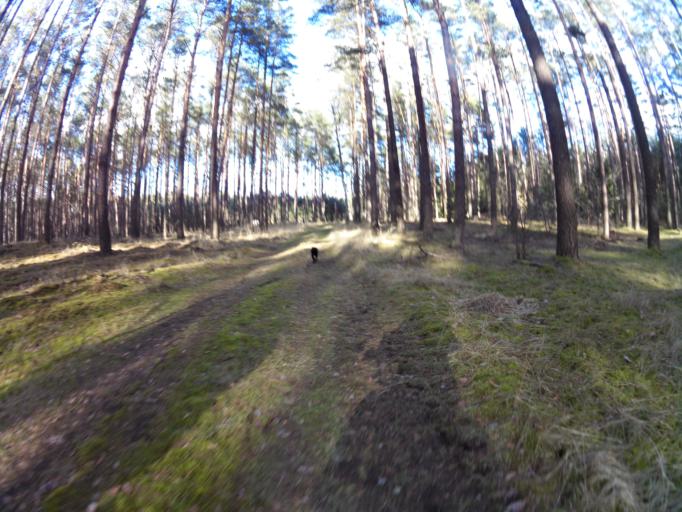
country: PL
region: West Pomeranian Voivodeship
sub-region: Powiat mysliborski
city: Debno
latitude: 52.7861
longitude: 14.7450
